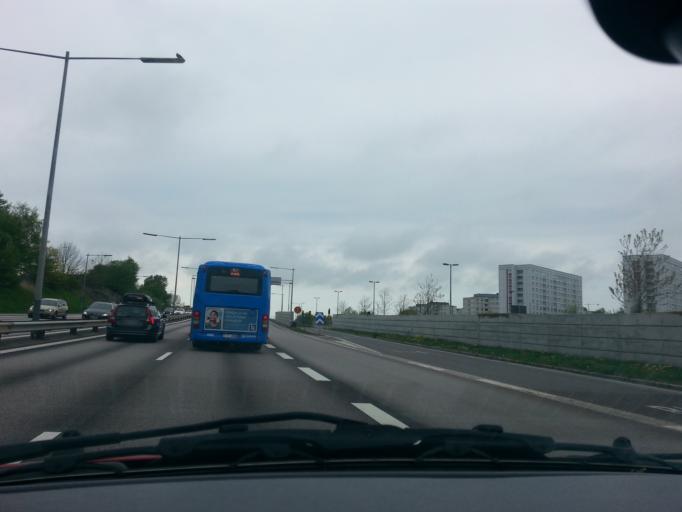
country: SE
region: Vaestra Goetaland
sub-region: Goteborg
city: Majorna
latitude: 57.6503
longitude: 11.9099
